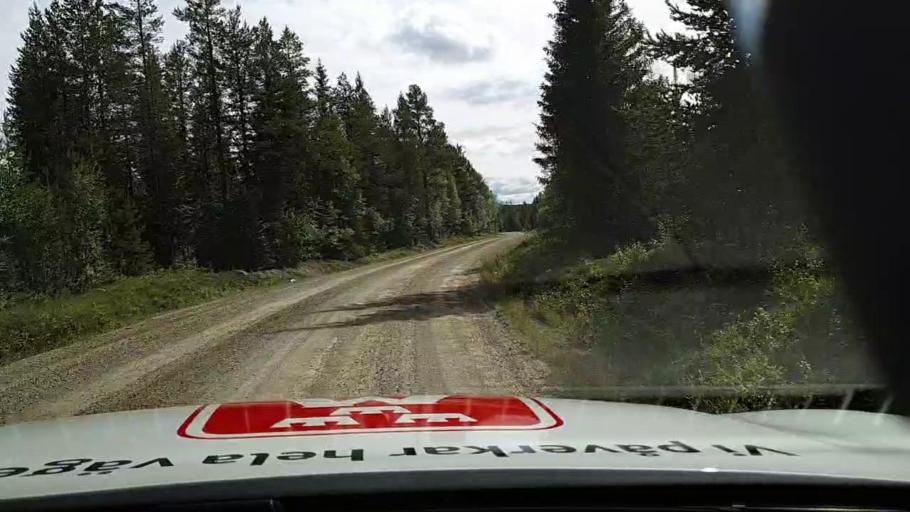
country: SE
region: Jaemtland
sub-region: Are Kommun
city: Jarpen
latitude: 62.5433
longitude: 13.4739
